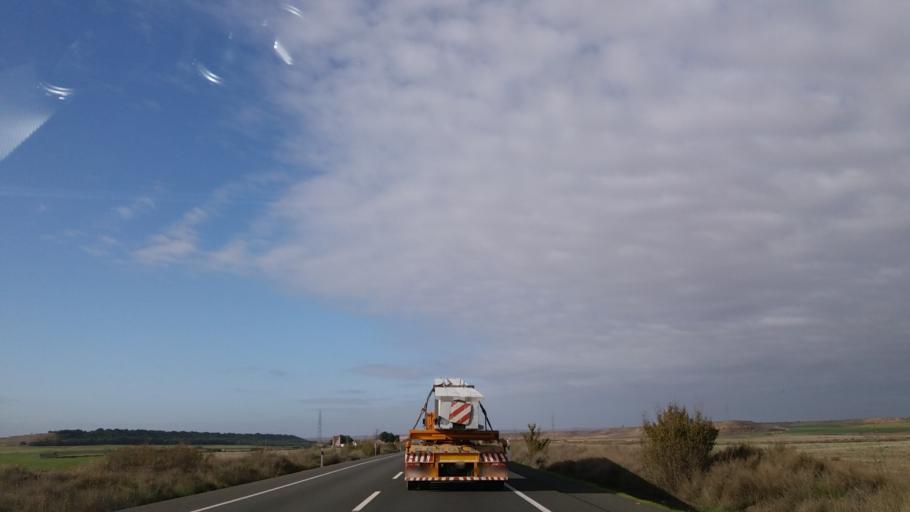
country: ES
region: Aragon
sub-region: Provincia de Huesca
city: Saidi / Zaidin
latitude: 41.5193
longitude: 0.2134
